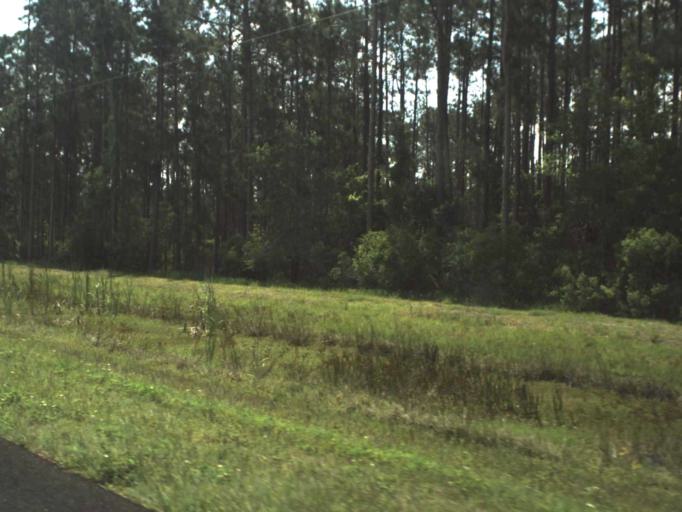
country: US
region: Florida
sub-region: Volusia County
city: Glencoe
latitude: 29.0123
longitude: -81.0059
